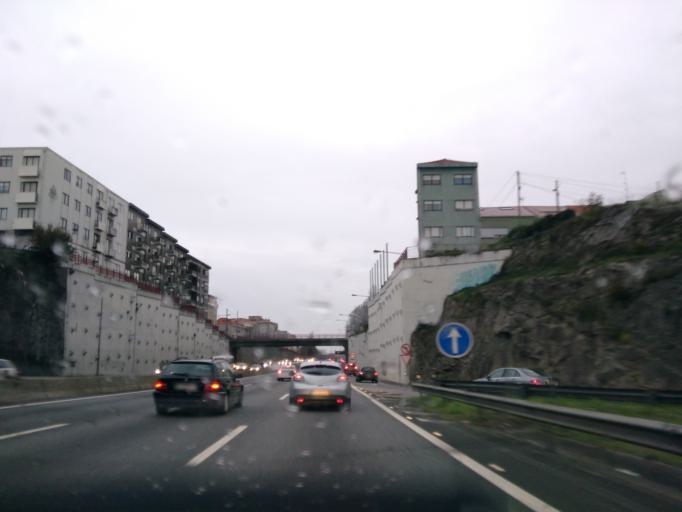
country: PT
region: Porto
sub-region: Maia
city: Pedroucos
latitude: 41.1684
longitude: -8.5891
